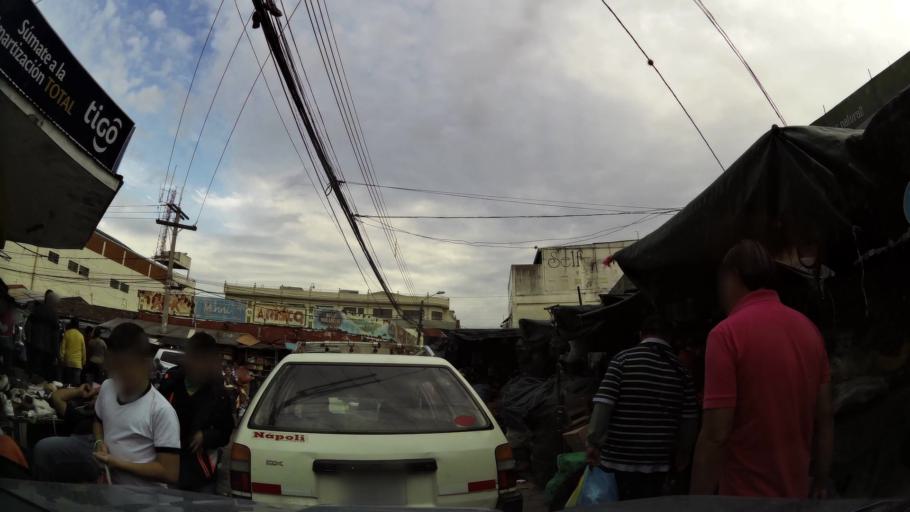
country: BO
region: Santa Cruz
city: Santa Cruz de la Sierra
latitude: -17.7776
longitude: -63.1773
